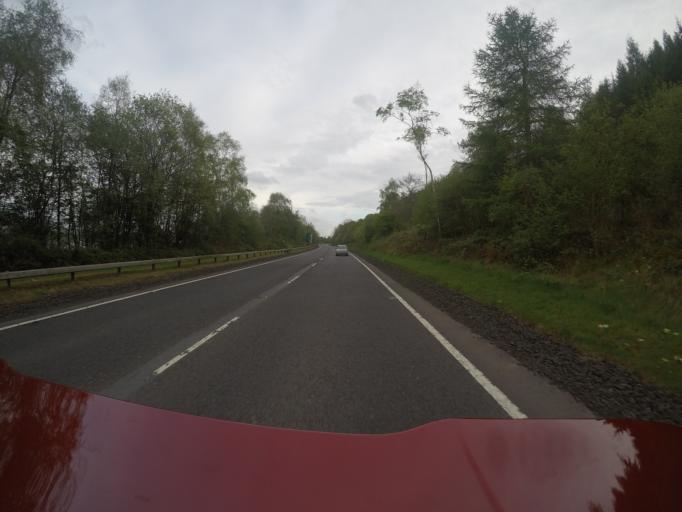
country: GB
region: Scotland
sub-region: West Dunbartonshire
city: Balloch
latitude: 56.1119
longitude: -4.6423
